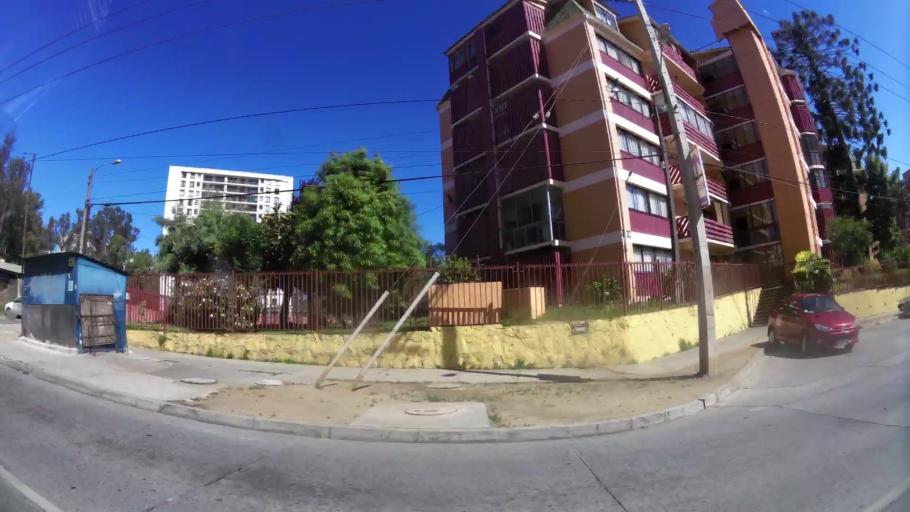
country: CL
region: Valparaiso
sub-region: Provincia de Valparaiso
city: Valparaiso
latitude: -33.0569
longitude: -71.5865
